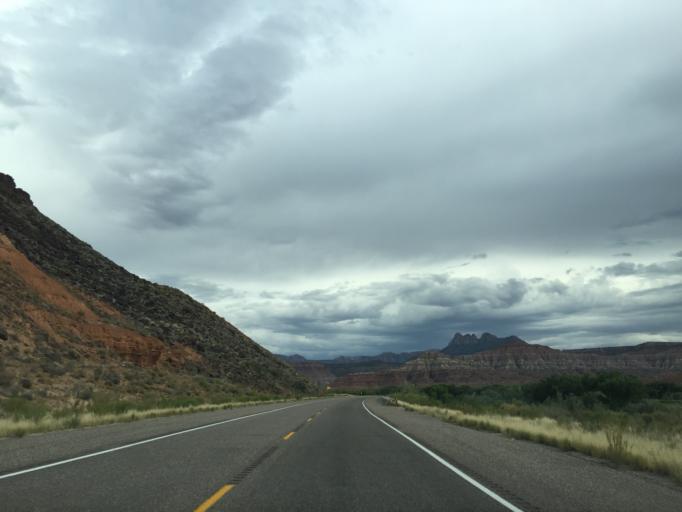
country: US
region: Utah
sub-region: Washington County
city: LaVerkin
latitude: 37.1870
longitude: -113.1387
